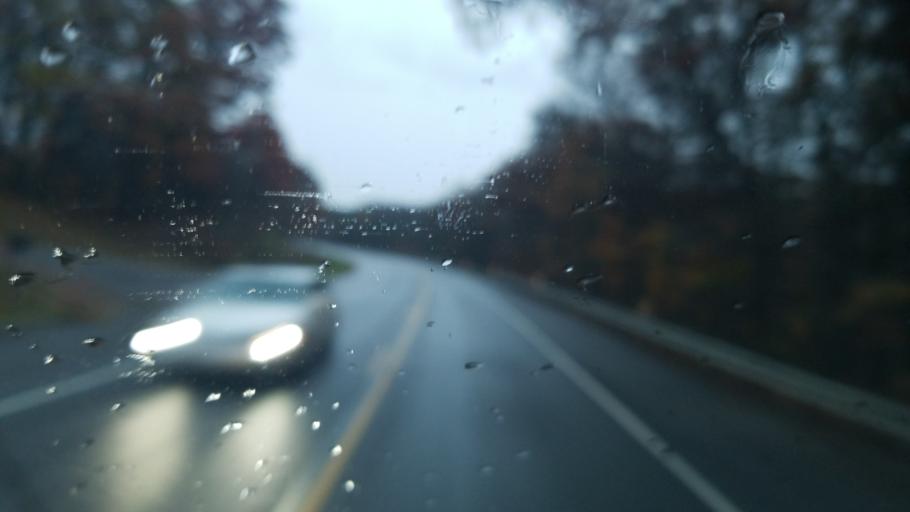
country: US
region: Pennsylvania
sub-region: Clarion County
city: Marianne
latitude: 41.2038
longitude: -79.4276
